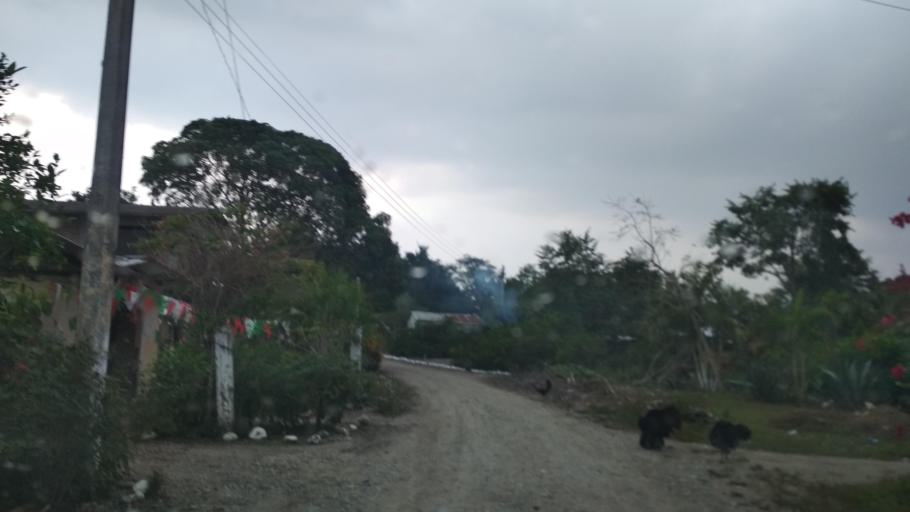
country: MM
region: Shan
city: Taunggyi
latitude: 20.3197
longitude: 97.3034
